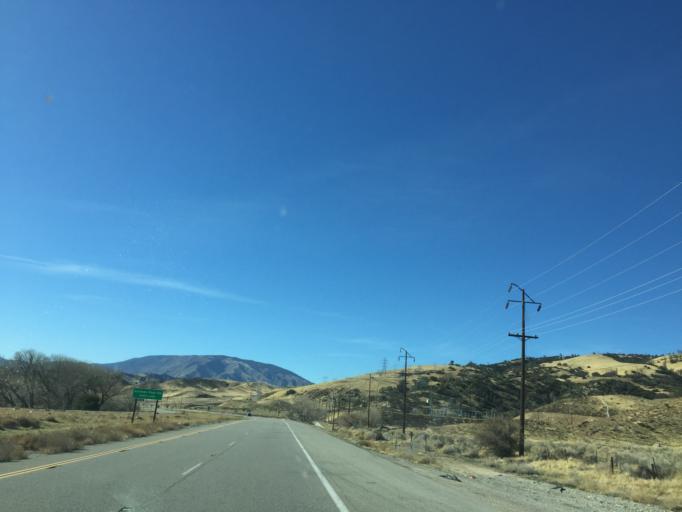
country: US
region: California
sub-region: Kern County
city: Lebec
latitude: 34.7743
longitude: -118.7686
